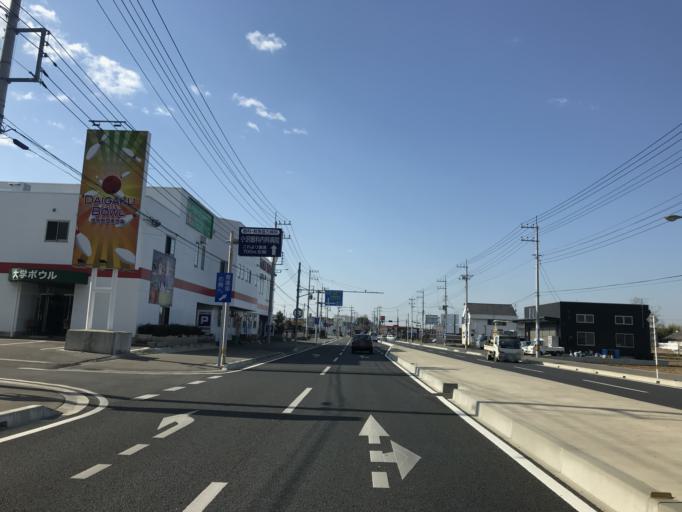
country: JP
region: Ibaraki
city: Mito-shi
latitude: 36.3386
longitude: 140.4622
